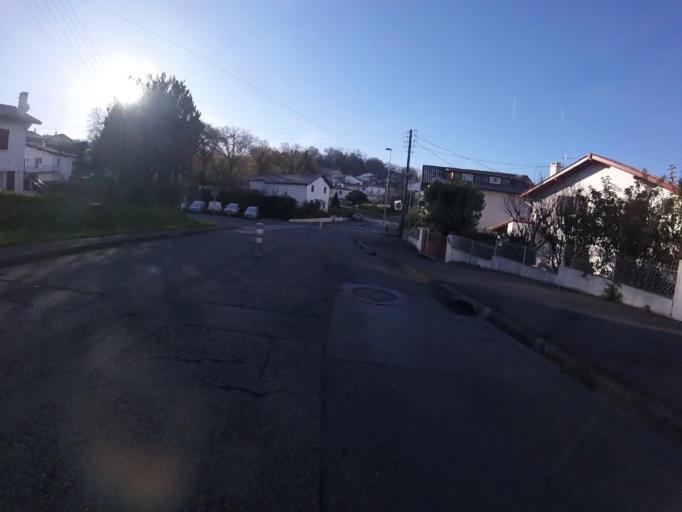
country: FR
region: Aquitaine
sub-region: Departement des Pyrenees-Atlantiques
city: Hendaye
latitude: 43.3571
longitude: -1.7659
